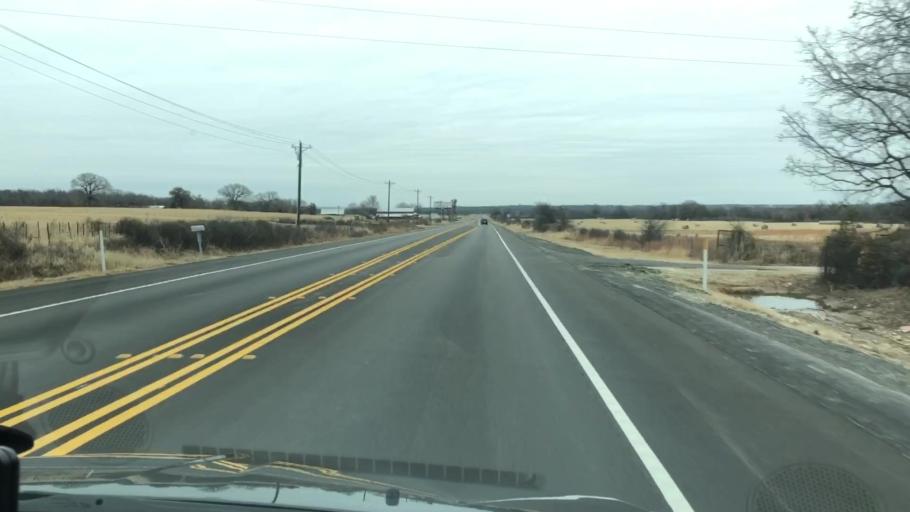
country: US
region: Texas
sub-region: Palo Pinto County
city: Mineral Wells
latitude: 32.5331
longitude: -98.1239
